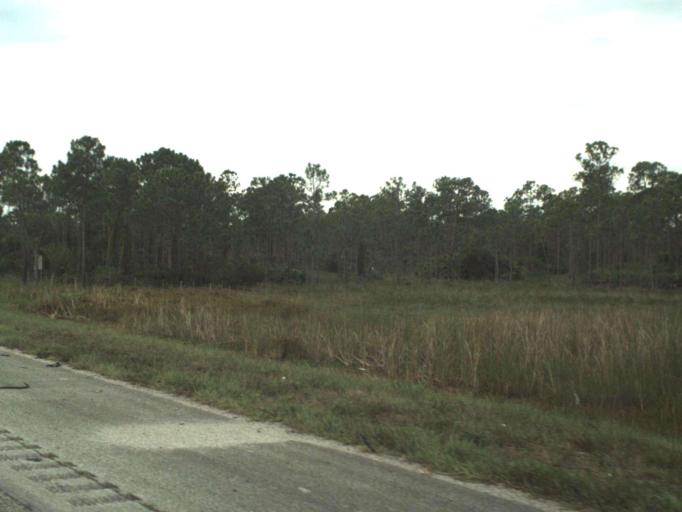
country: US
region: Florida
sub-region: Martin County
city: Palm City
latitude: 27.1303
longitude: -80.3517
